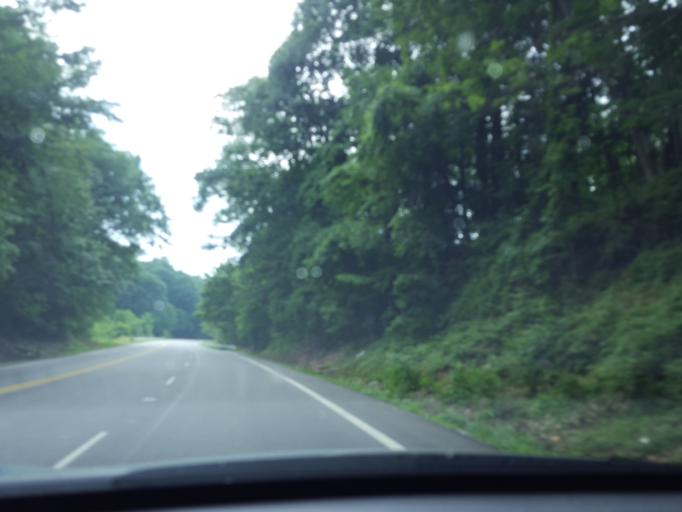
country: US
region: Virginia
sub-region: City of Waynesboro
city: Waynesboro
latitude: 38.0426
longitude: -78.8571
